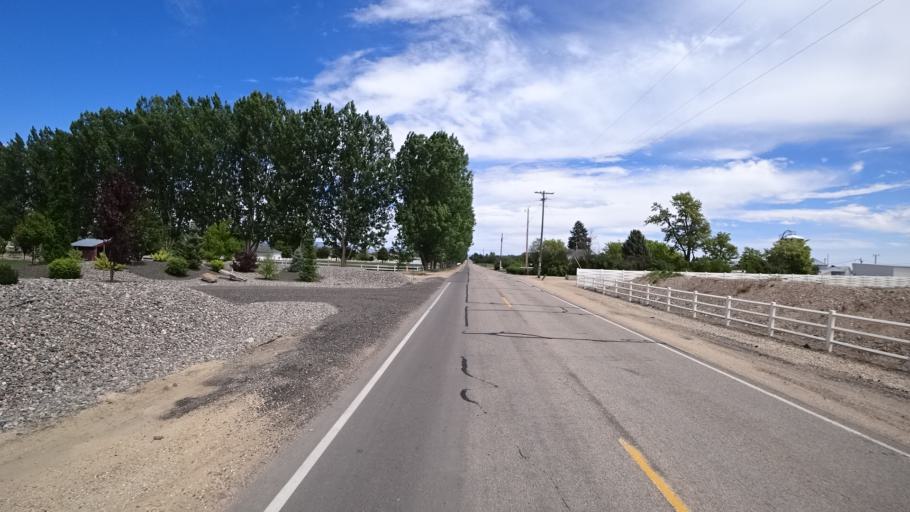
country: US
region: Idaho
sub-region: Ada County
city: Meridian
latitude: 43.5757
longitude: -116.4245
